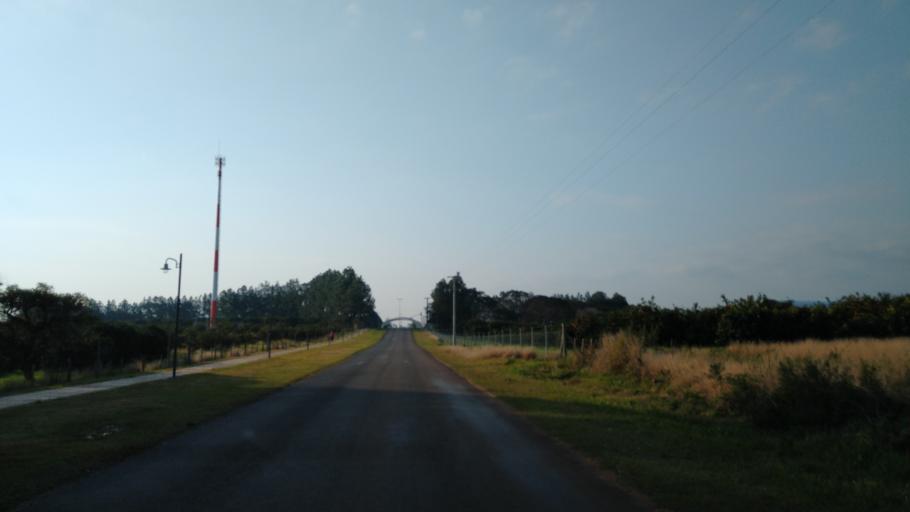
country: AR
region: Entre Rios
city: Santa Ana
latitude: -30.9026
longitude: -57.9247
